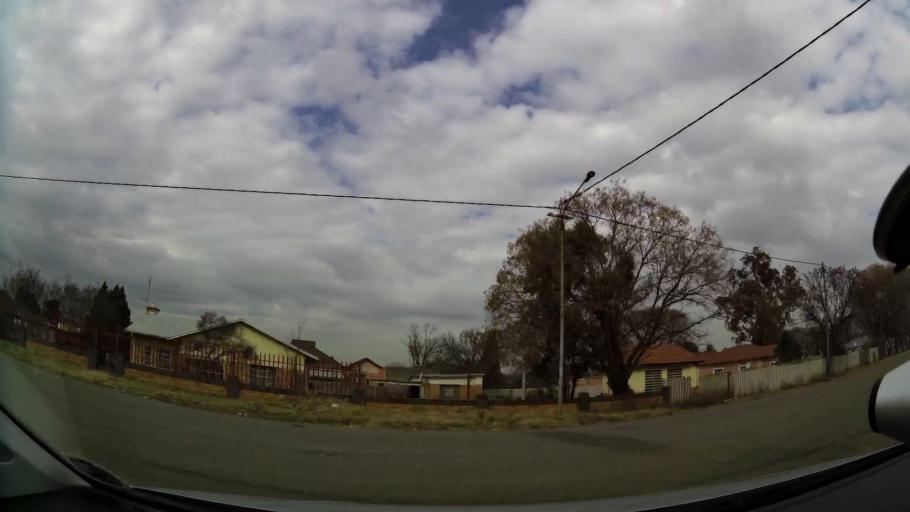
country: ZA
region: Orange Free State
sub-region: Fezile Dabi District Municipality
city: Kroonstad
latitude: -27.6556
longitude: 27.2342
